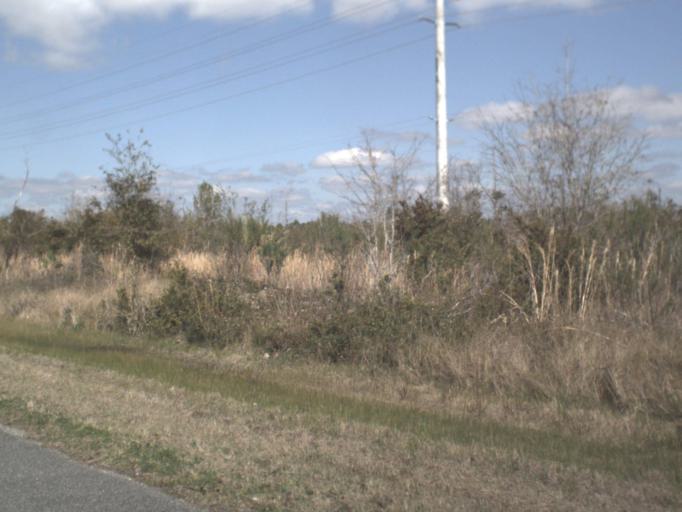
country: US
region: Florida
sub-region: Franklin County
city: Apalachicola
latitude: 29.7201
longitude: -85.0667
